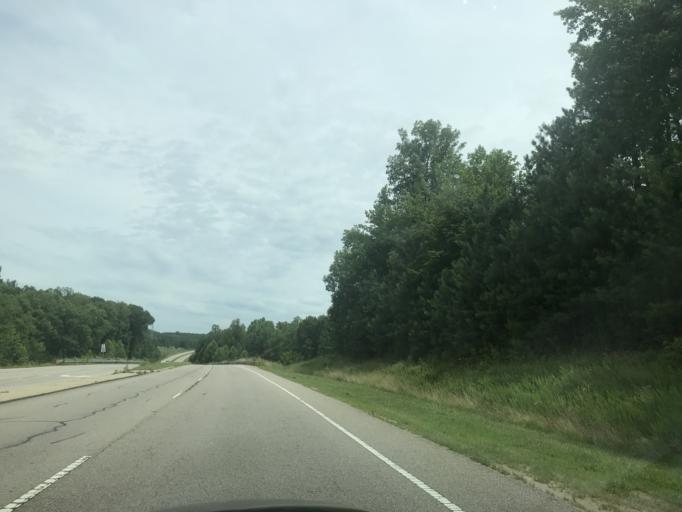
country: US
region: North Carolina
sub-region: Vance County
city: South Henderson
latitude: 36.3062
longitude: -78.4410
